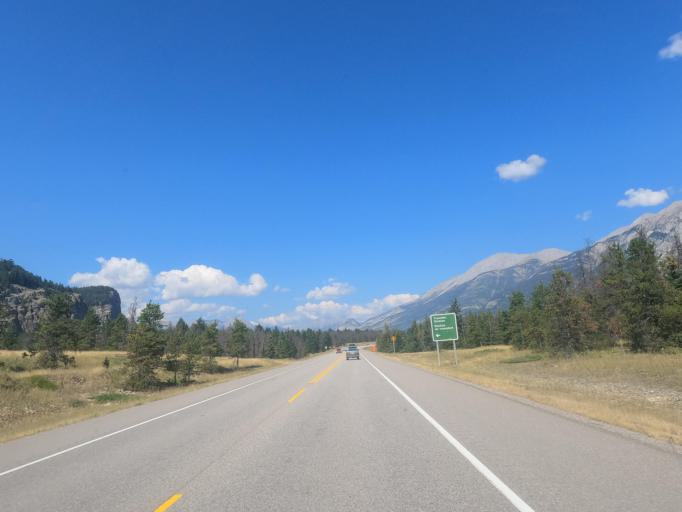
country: CA
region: Alberta
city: Jasper Park Lodge
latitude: 52.9359
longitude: -118.0386
